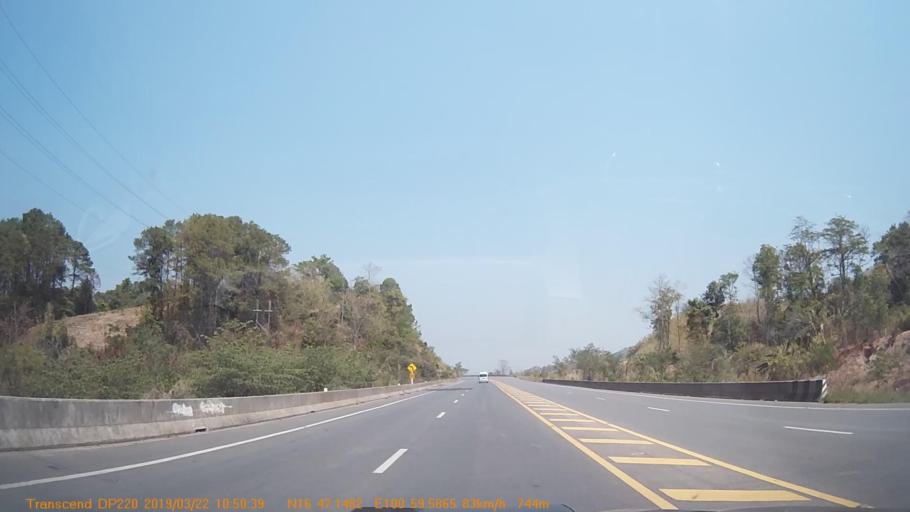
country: TH
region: Phetchabun
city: Khao Kho
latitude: 16.7860
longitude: 100.9930
